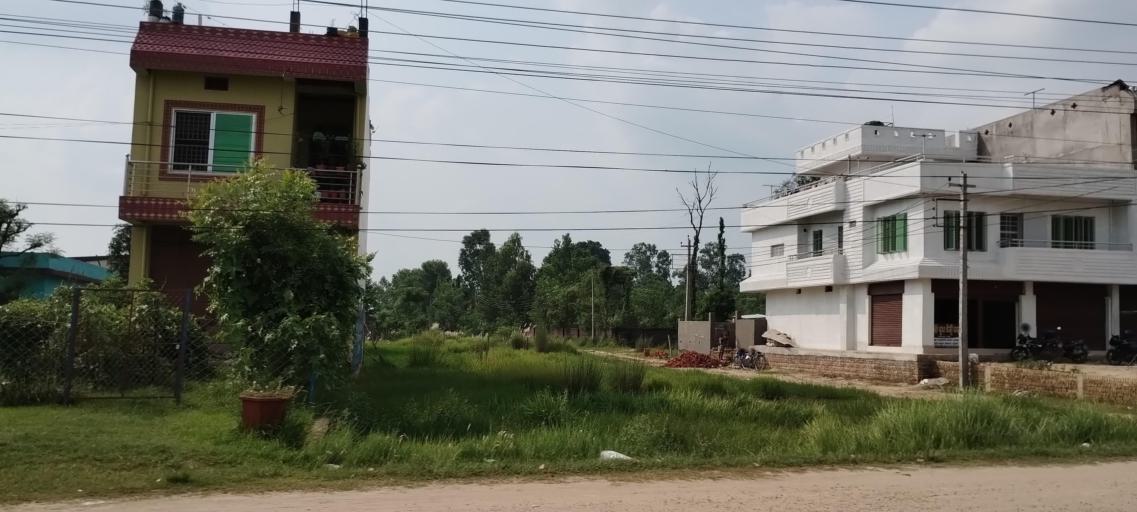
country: NP
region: Mid Western
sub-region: Bheri Zone
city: Nepalgunj
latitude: 28.1672
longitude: 81.6748
